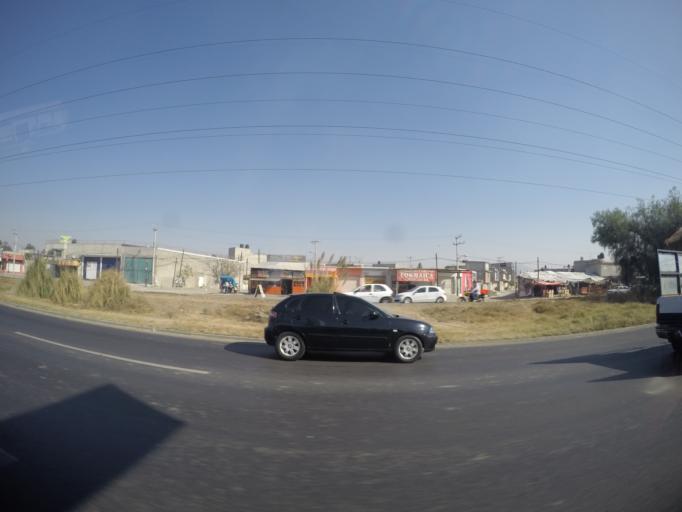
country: MX
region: Mexico
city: Santo Tomas Chiconautla
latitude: 19.6131
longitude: -99.0099
